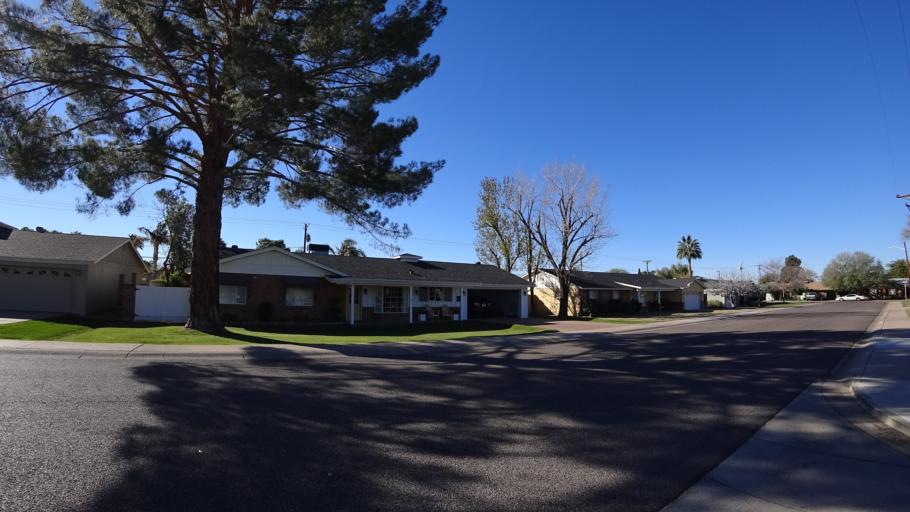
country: US
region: Arizona
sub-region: Maricopa County
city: Paradise Valley
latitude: 33.5067
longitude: -112.0071
